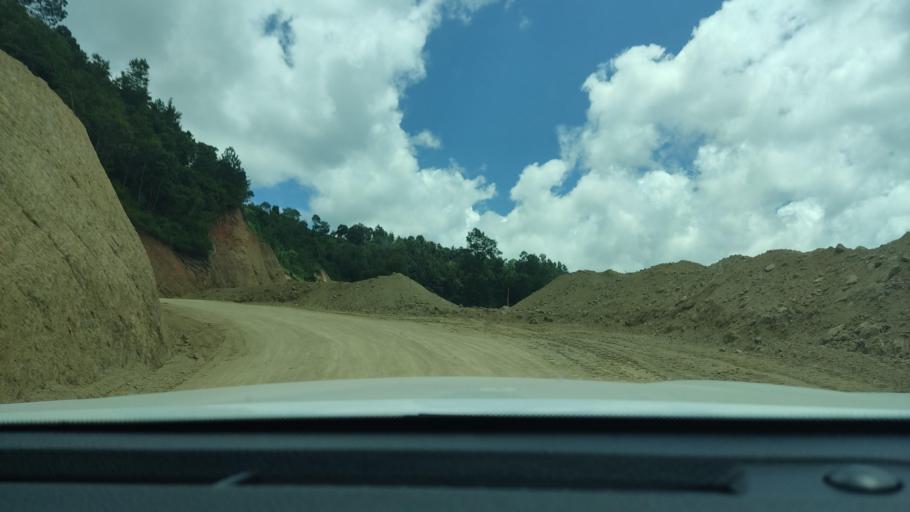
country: GT
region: Chimaltenango
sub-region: Municipio de San Juan Comalapa
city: Comalapa
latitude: 14.7833
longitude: -90.8670
